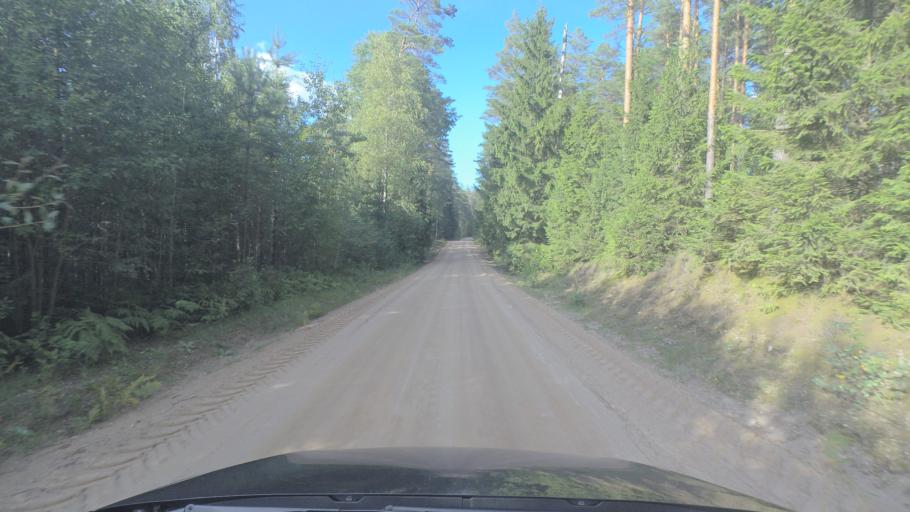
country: LT
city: Pabrade
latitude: 55.1635
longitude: 25.8288
